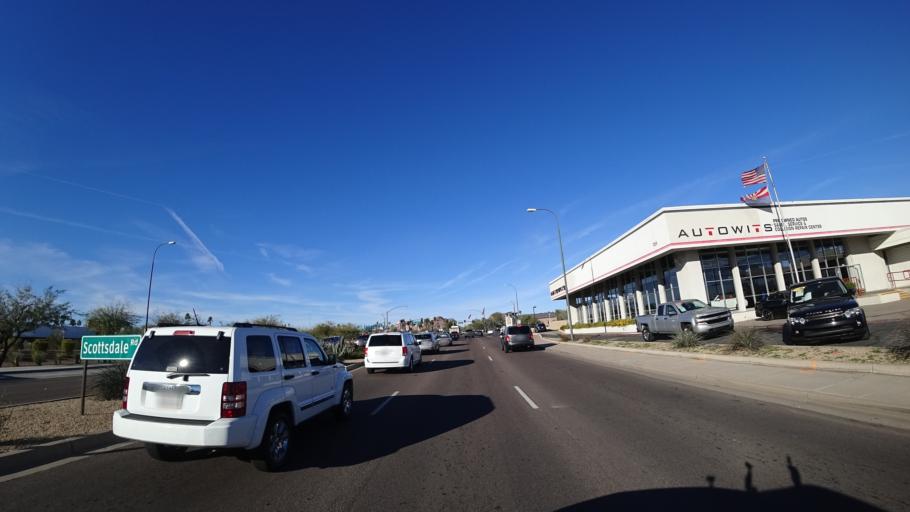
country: US
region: Arizona
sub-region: Maricopa County
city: Scottsdale
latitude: 33.4658
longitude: -111.9247
